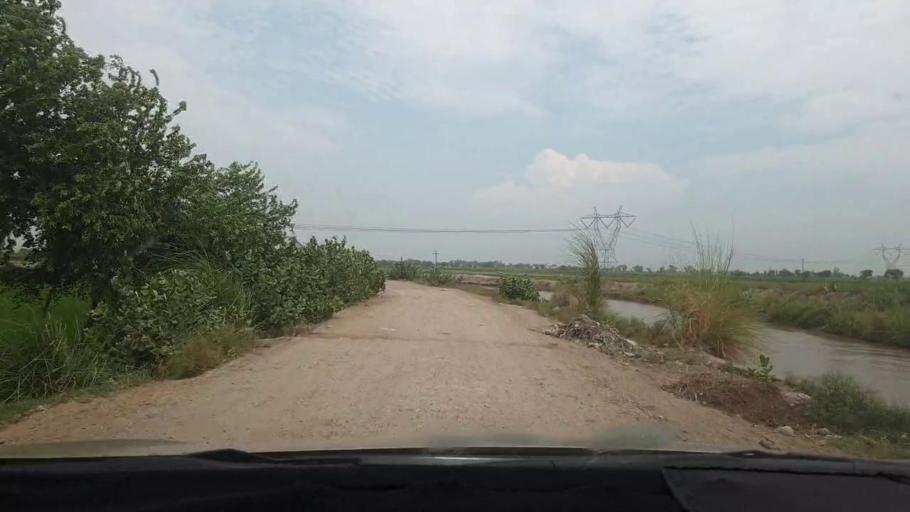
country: PK
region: Sindh
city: Naudero
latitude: 27.6795
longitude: 68.3399
